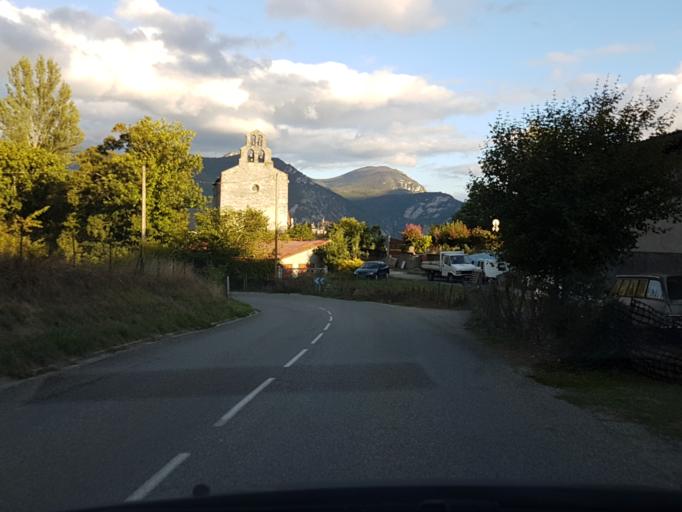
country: FR
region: Midi-Pyrenees
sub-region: Departement de l'Ariege
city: Tarascon-sur-Ariege
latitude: 42.8588
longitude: 1.5768
